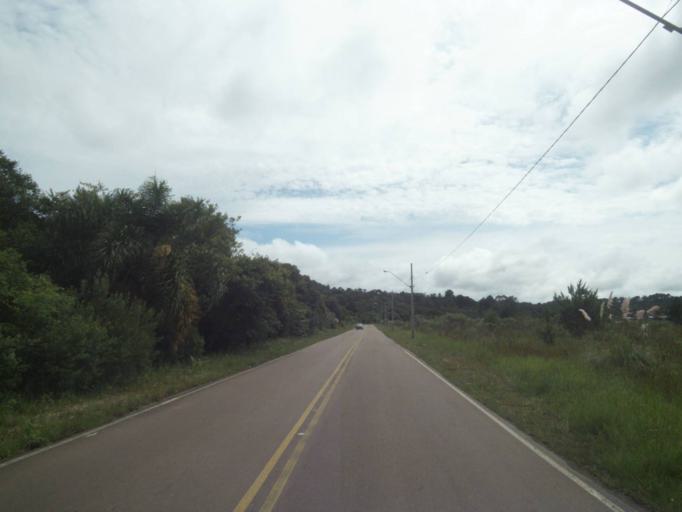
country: BR
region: Parana
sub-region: Campina Grande Do Sul
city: Campina Grande do Sul
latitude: -25.3138
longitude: -49.0200
